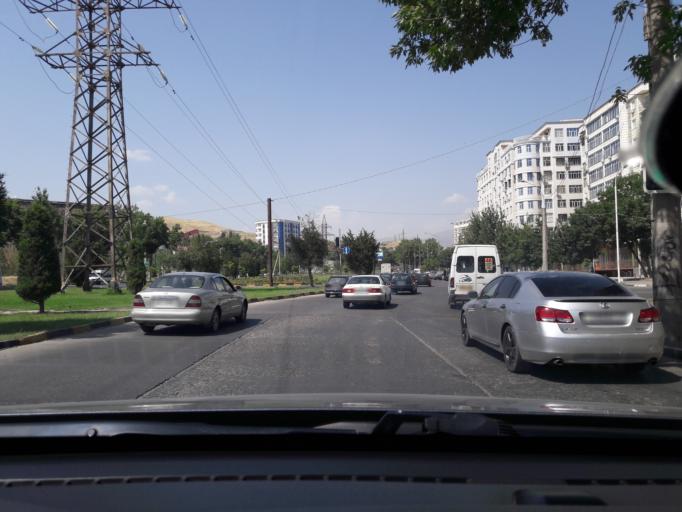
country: TJ
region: Dushanbe
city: Dushanbe
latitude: 38.5896
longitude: 68.7415
